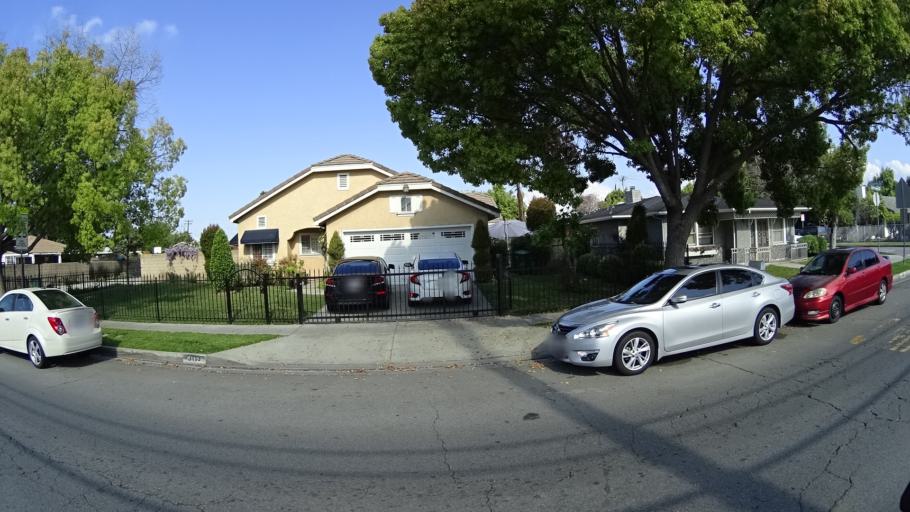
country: US
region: California
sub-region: Los Angeles County
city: Baldwin Park
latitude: 34.0710
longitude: -117.9697
